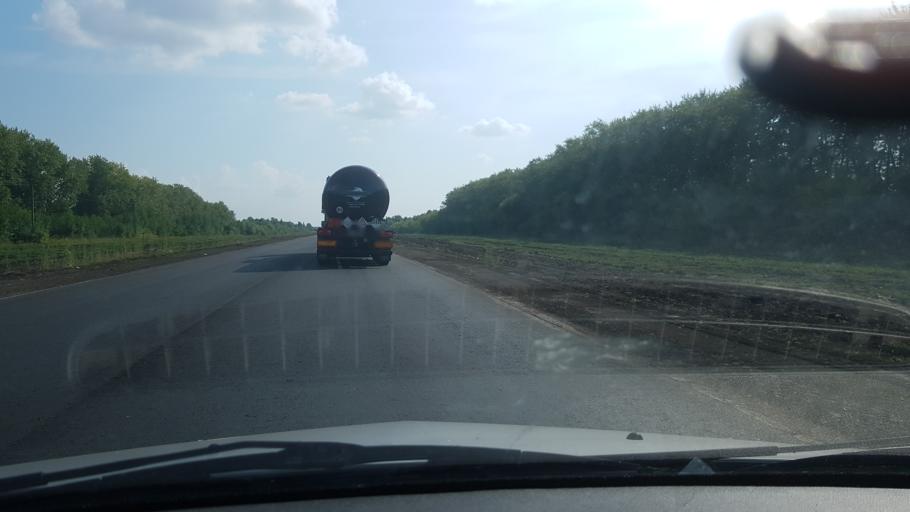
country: RU
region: Chuvashia
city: Shikhazany
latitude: 55.7083
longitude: 47.4401
